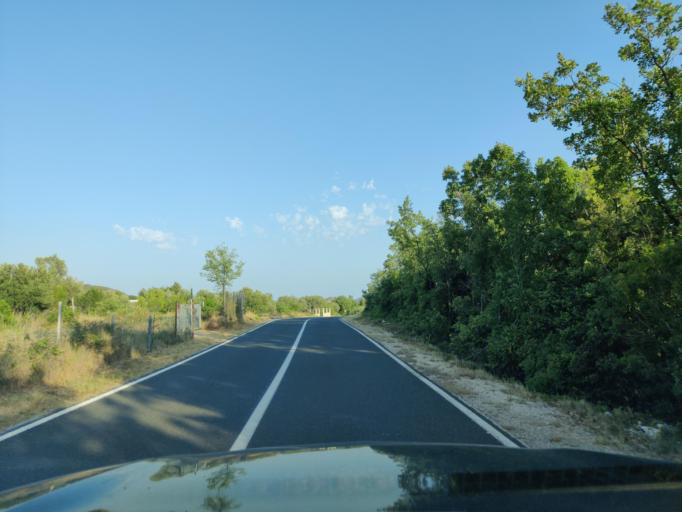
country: HR
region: Sibensko-Kniniska
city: Tribunj
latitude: 43.7733
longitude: 15.7245
